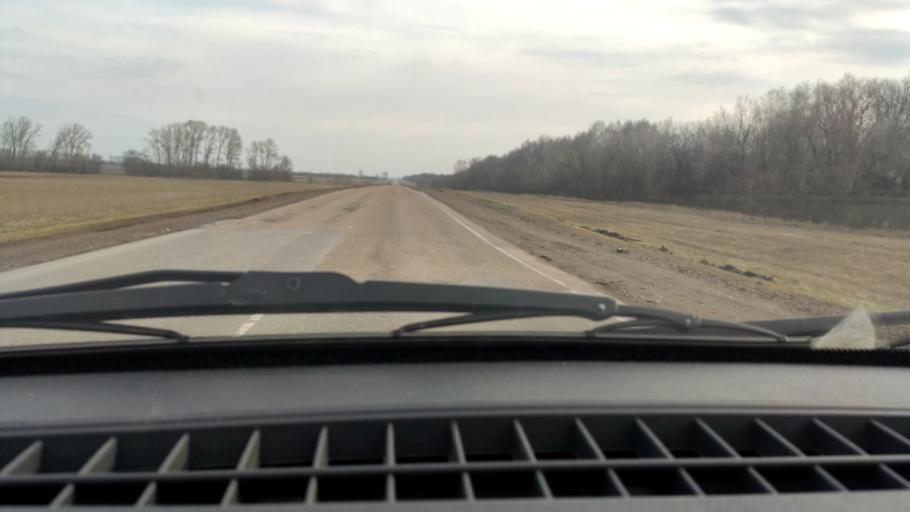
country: RU
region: Bashkortostan
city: Davlekanovo
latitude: 54.2552
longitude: 55.0849
